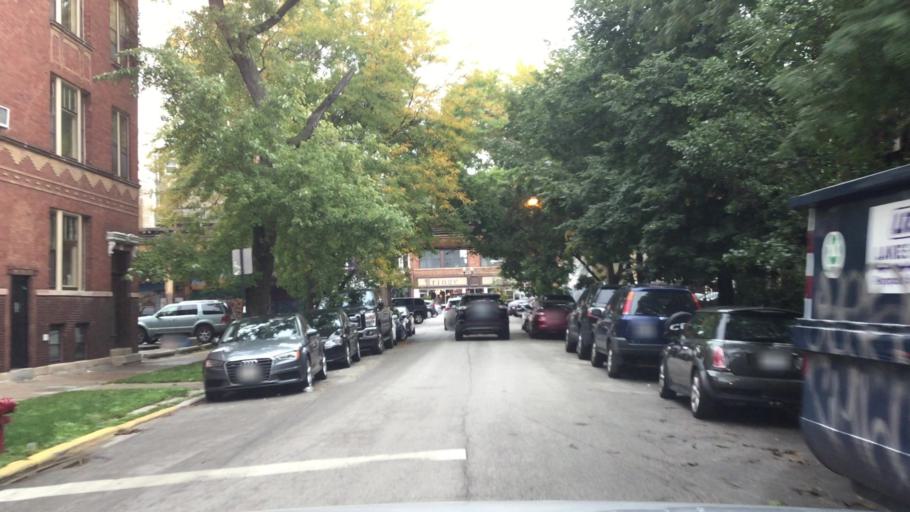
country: US
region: Illinois
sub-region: Cook County
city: Chicago
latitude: 41.9072
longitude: -87.6746
